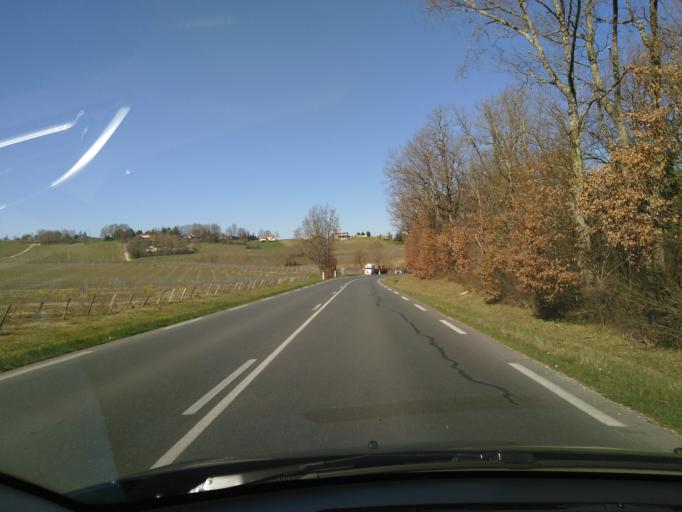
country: FR
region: Aquitaine
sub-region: Departement de la Dordogne
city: Monbazillac
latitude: 44.7847
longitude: 0.5248
